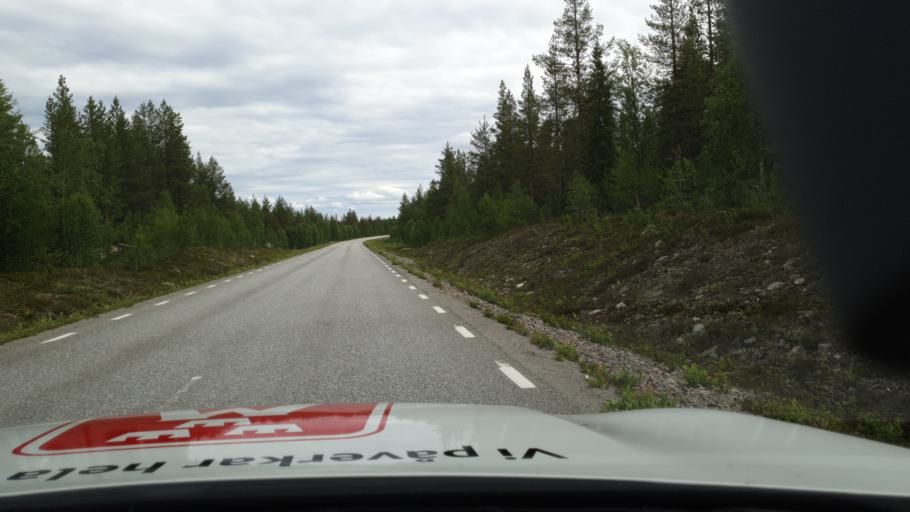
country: SE
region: Vaesterbotten
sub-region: Storumans Kommun
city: Storuman
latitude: 65.5174
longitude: 17.0955
